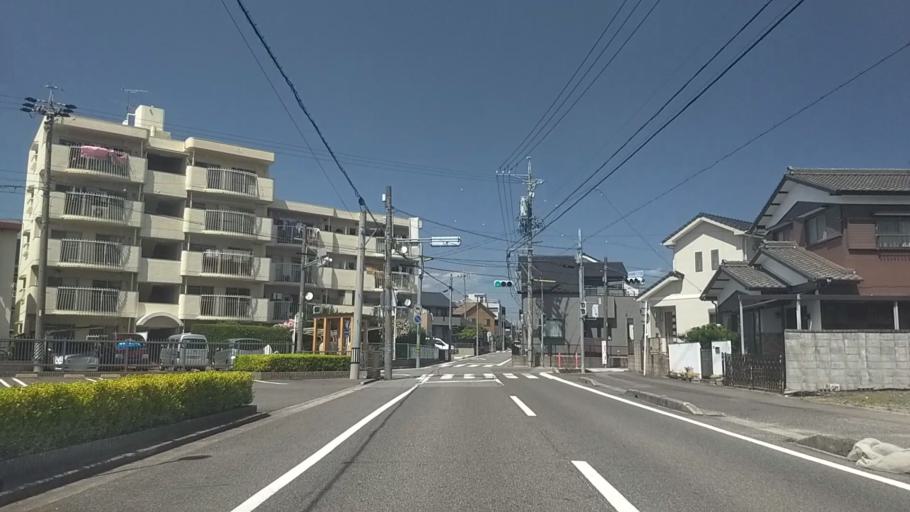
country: JP
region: Aichi
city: Okazaki
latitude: 34.9754
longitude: 137.1719
